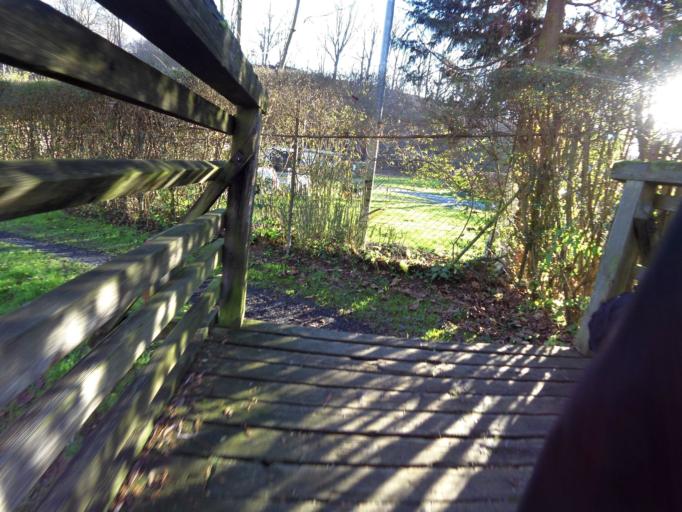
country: DE
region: Lower Saxony
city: Buhren
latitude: 51.4740
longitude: 9.6225
